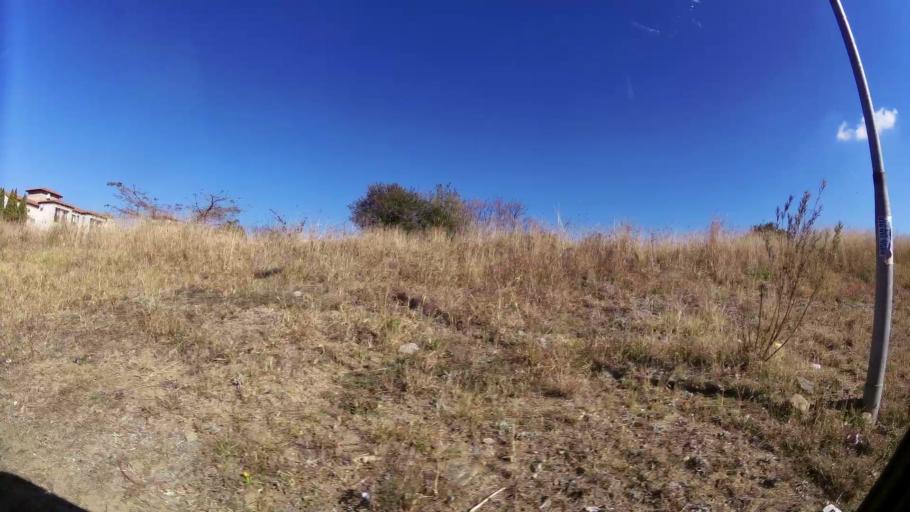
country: ZA
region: Gauteng
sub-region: West Rand District Municipality
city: Muldersdriseloop
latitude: -26.0490
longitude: 27.9599
